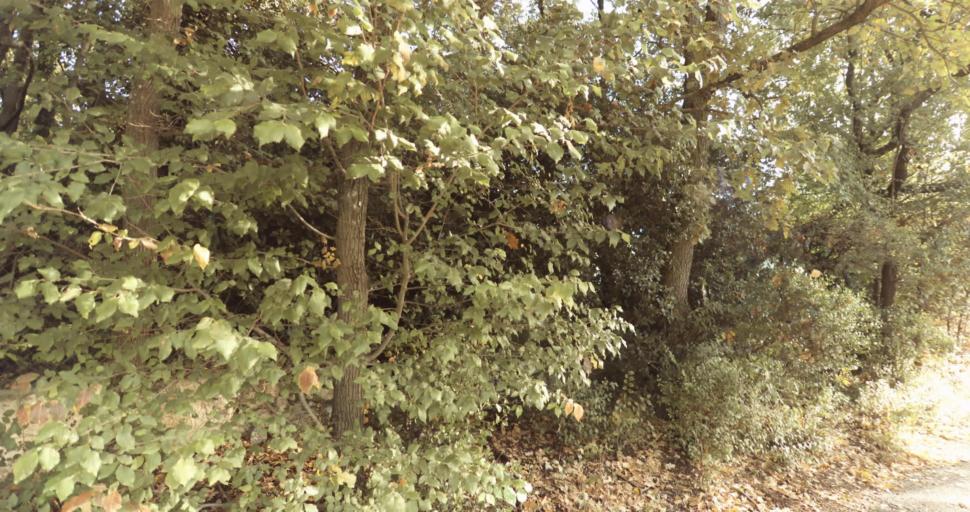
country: FR
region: Provence-Alpes-Cote d'Azur
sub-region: Departement des Bouches-du-Rhone
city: Venelles
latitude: 43.5901
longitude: 5.4666
